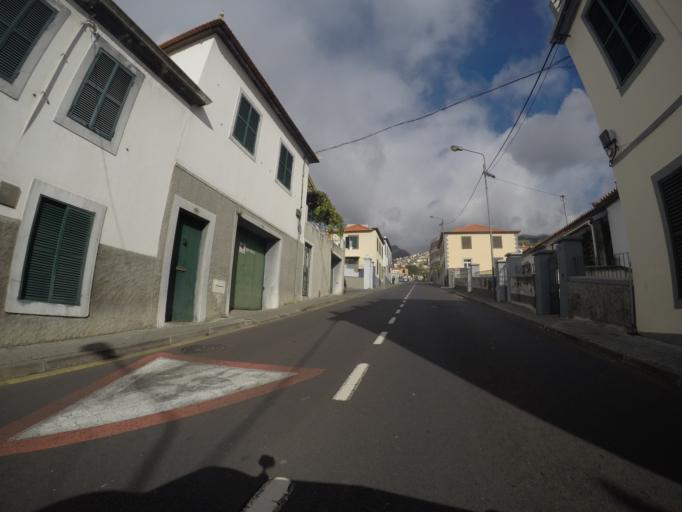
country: PT
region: Madeira
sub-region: Funchal
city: Nossa Senhora do Monte
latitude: 32.6565
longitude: -16.9127
